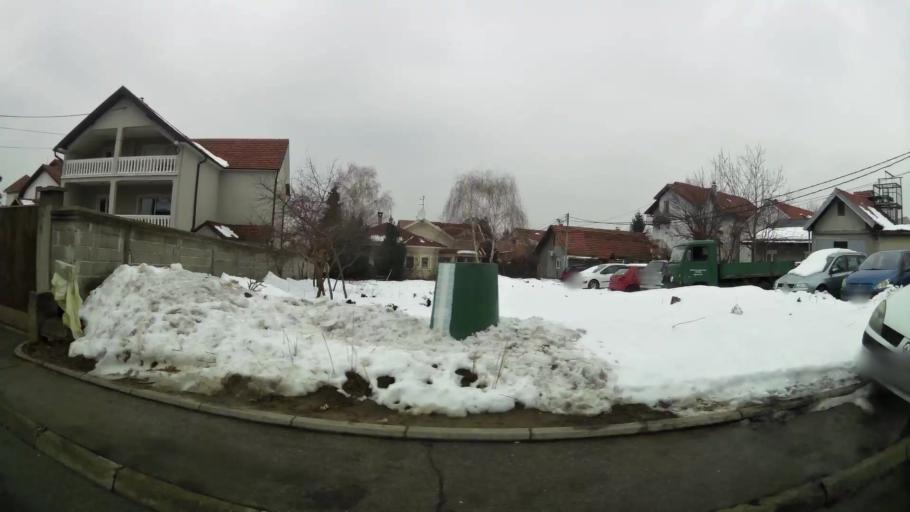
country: RS
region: Central Serbia
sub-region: Belgrade
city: Zvezdara
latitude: 44.7659
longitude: 20.5044
